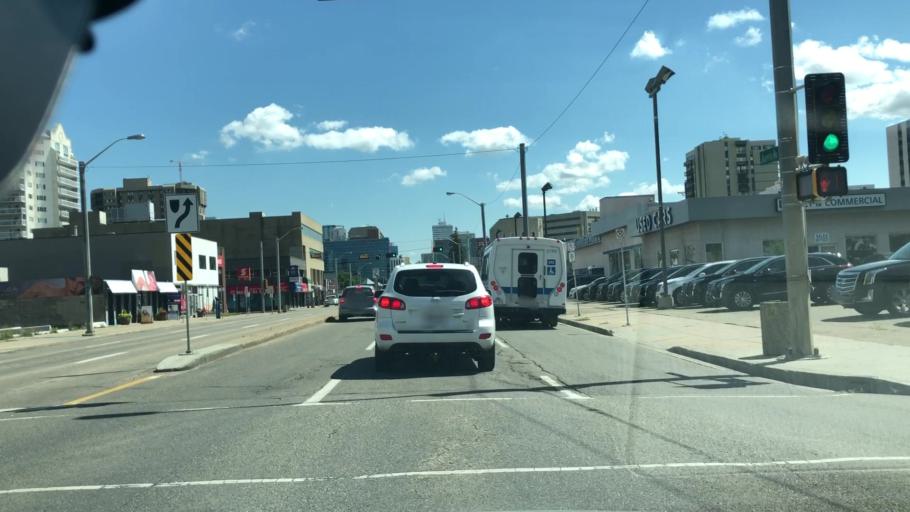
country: CA
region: Alberta
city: Edmonton
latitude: 53.5409
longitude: -113.5212
